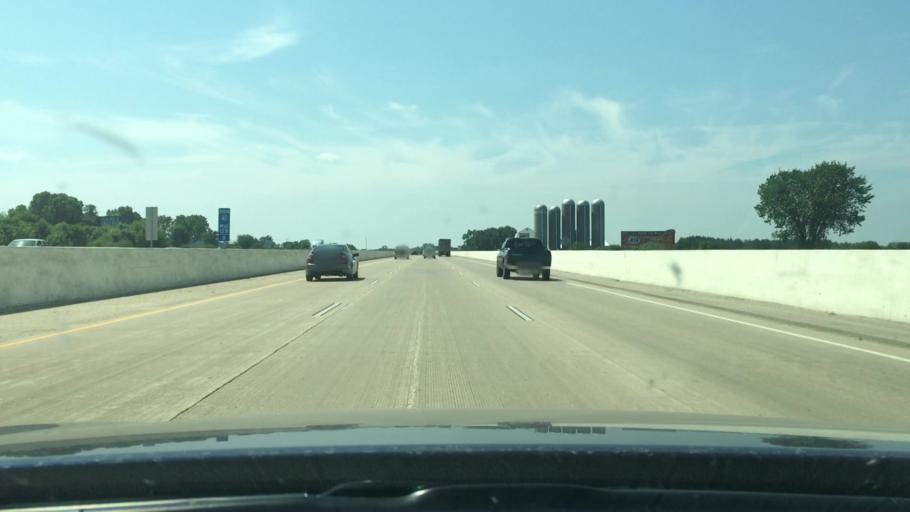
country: US
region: Wisconsin
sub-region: Winnebago County
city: Neenah
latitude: 44.1395
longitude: -88.4921
